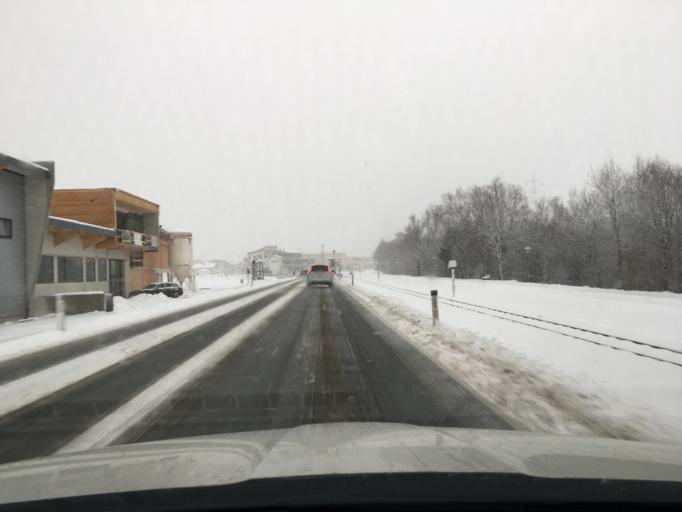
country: AT
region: Tyrol
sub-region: Politischer Bezirk Schwaz
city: Ramsau im Zillertal
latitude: 47.1962
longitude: 11.8711
